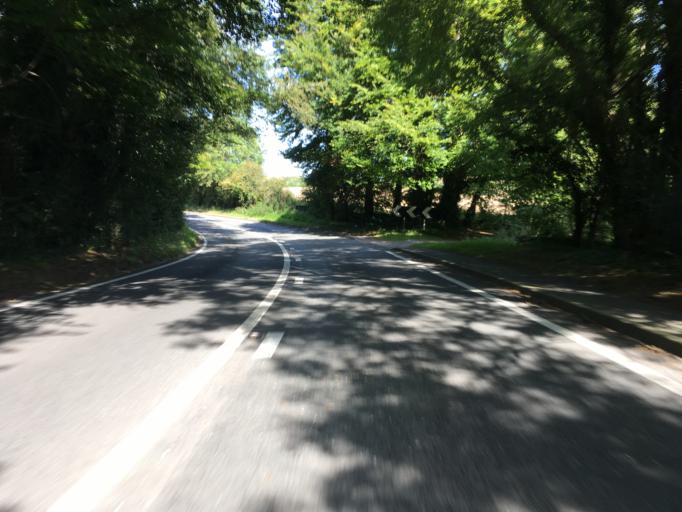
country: GB
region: England
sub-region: Hampshire
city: Compton
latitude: 51.0271
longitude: -1.3127
